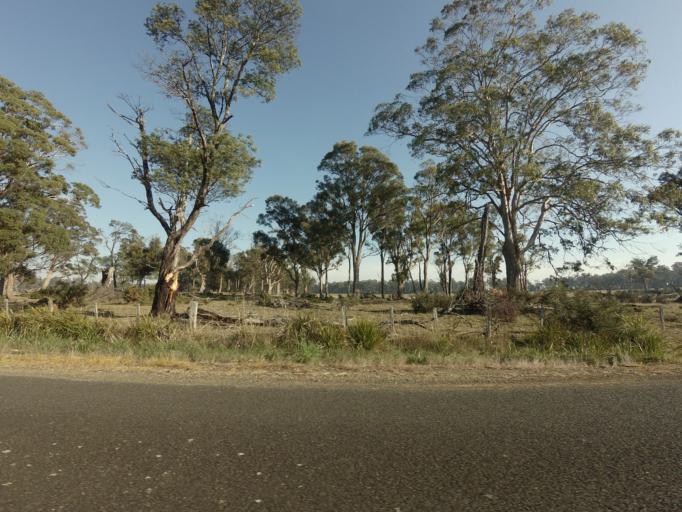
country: AU
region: Tasmania
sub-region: Northern Midlands
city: Longford
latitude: -41.5363
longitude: 146.9951
